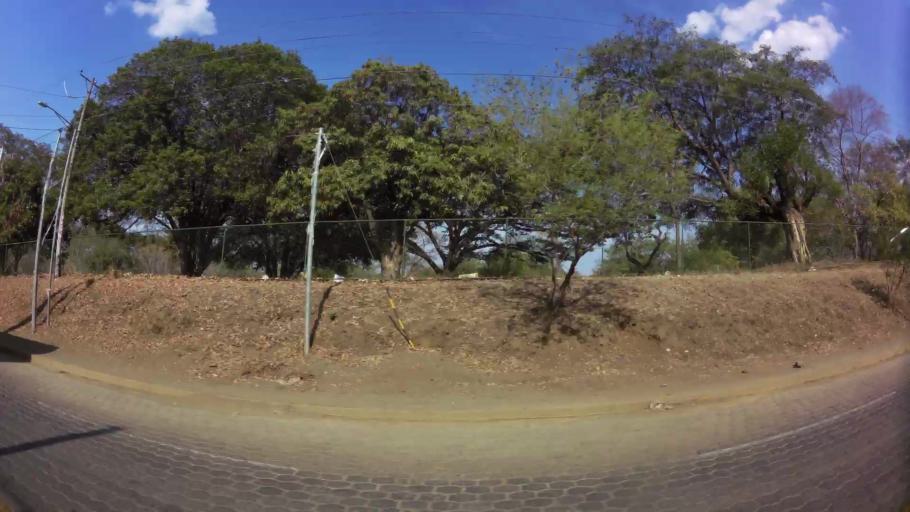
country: NI
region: Managua
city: Managua
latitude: 12.1098
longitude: -86.2718
